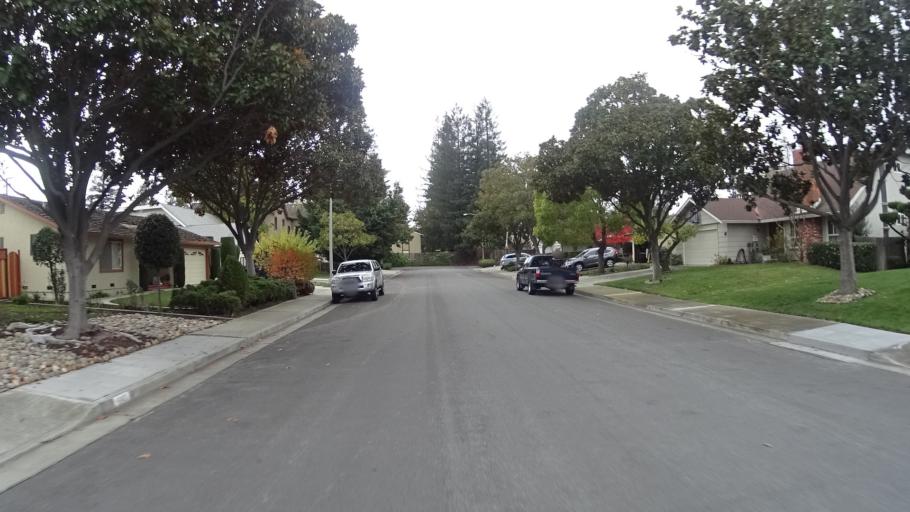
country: US
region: California
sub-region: Santa Clara County
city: Sunnyvale
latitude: 37.3603
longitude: -122.0018
